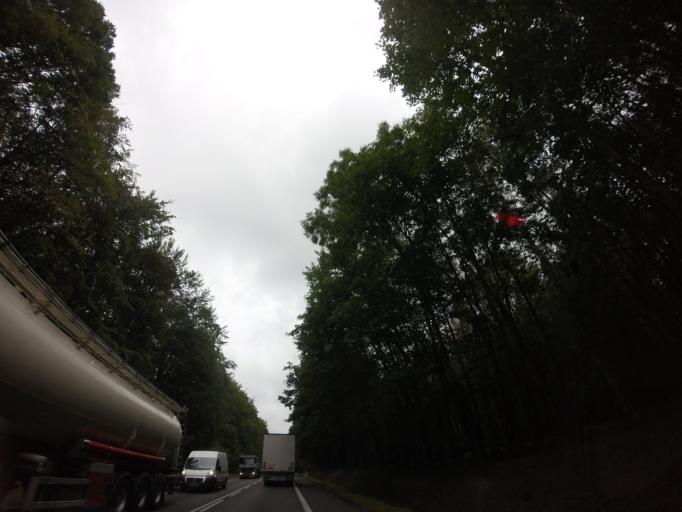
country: PL
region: West Pomeranian Voivodeship
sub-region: Powiat kamienski
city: Miedzyzdroje
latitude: 53.8841
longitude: 14.5077
